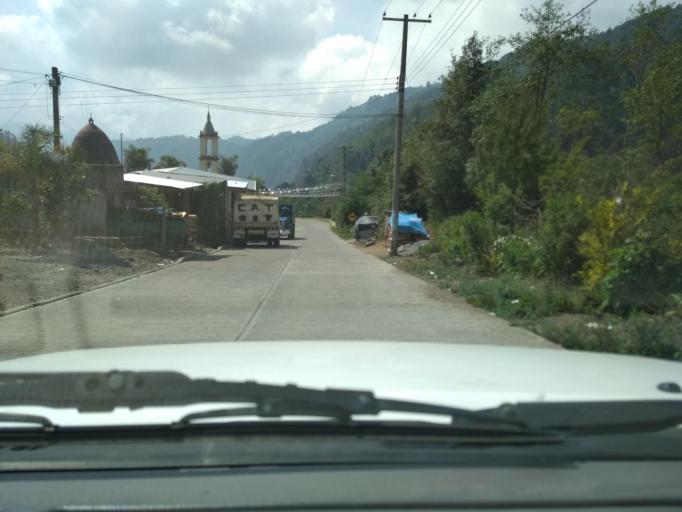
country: MX
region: Veracruz
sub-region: La Perla
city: Chilapa
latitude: 18.9897
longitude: -97.1818
